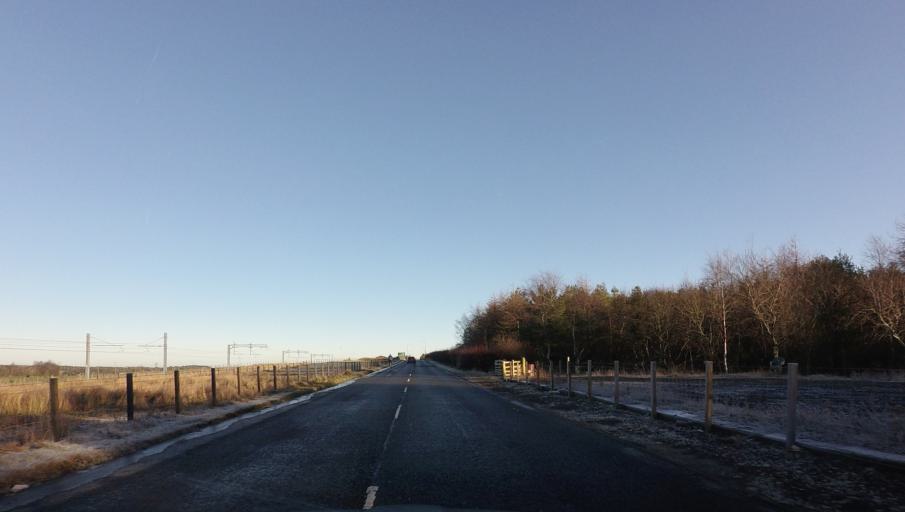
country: GB
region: Scotland
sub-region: West Lothian
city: Fauldhouse
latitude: 55.8251
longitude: -3.6742
